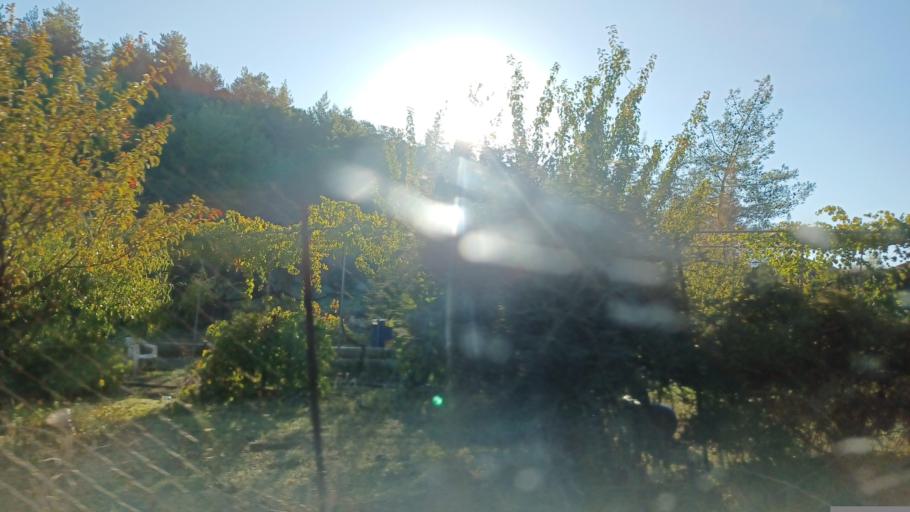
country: CY
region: Pafos
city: Mesogi
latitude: 34.9346
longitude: 32.5685
